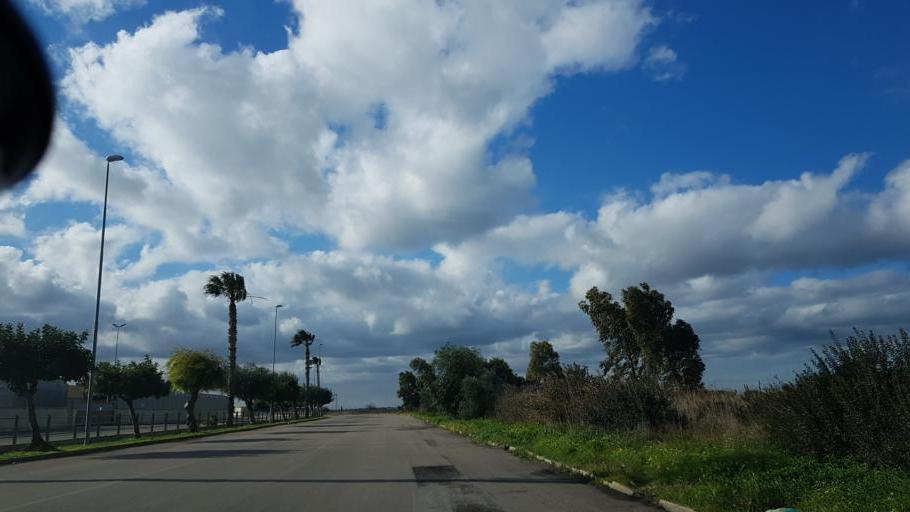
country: IT
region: Apulia
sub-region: Provincia di Brindisi
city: Brindisi
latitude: 40.6203
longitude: 17.9020
